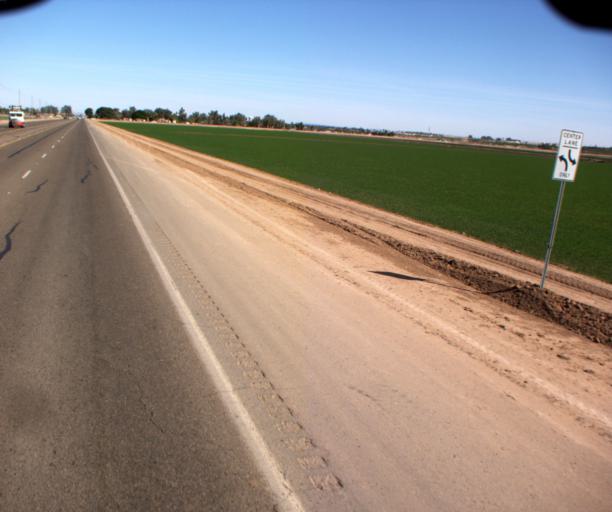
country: US
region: Arizona
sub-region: Yuma County
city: Somerton
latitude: 32.6277
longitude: -114.6498
